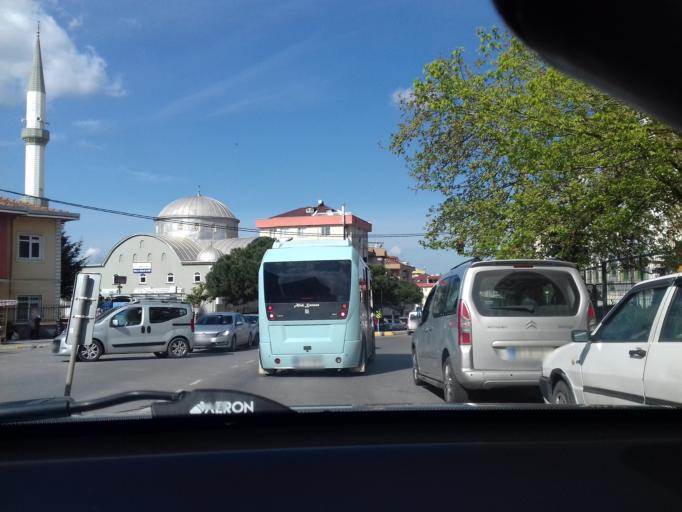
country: TR
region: Istanbul
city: Pendik
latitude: 40.9139
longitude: 29.2833
